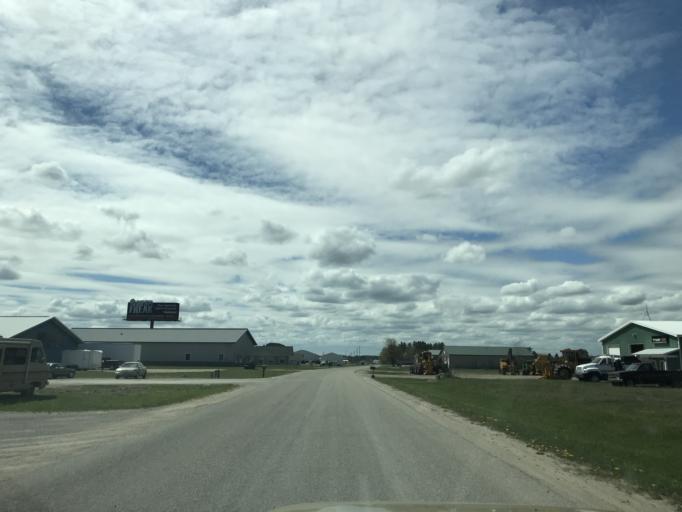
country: US
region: Michigan
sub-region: Otsego County
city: Gaylord
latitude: 45.0394
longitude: -84.6913
